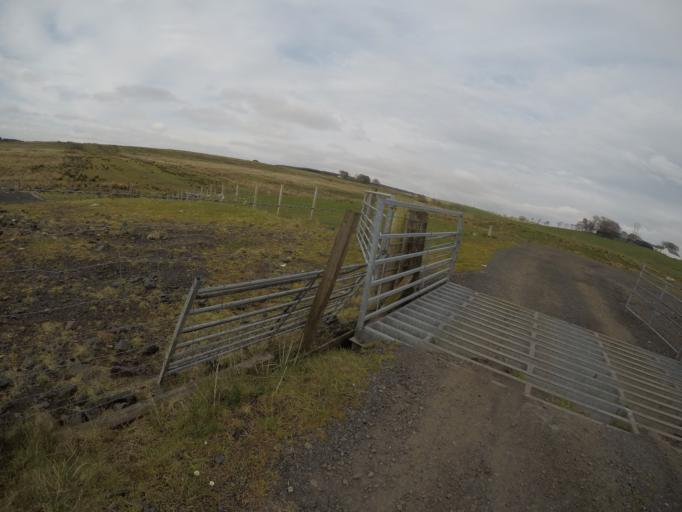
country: GB
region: Scotland
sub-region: East Ayrshire
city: Galston
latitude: 55.6873
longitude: -4.3938
